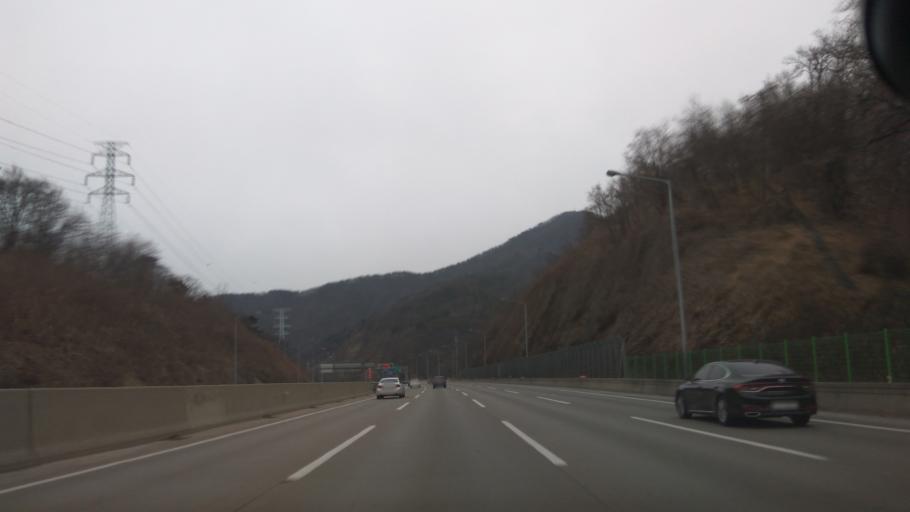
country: KR
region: Gyeonggi-do
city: Jangheung
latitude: 37.6822
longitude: 126.9264
